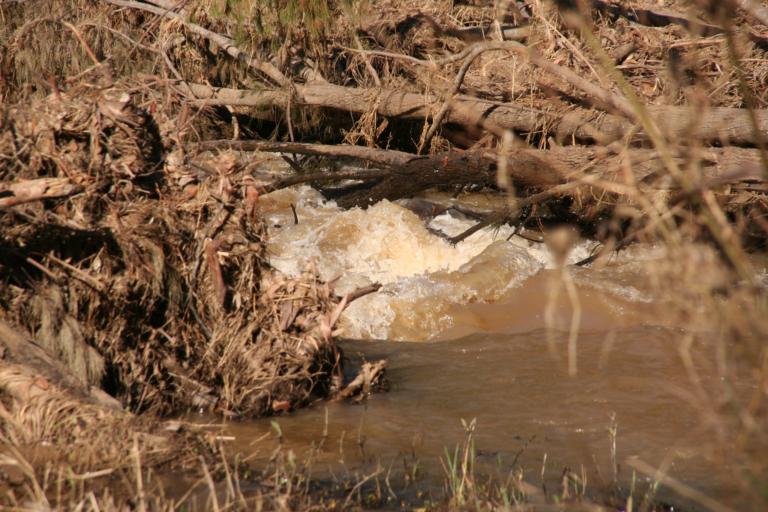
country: AU
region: Queensland
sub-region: Lockyer Valley
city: Gatton
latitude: -27.2422
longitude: 152.4243
